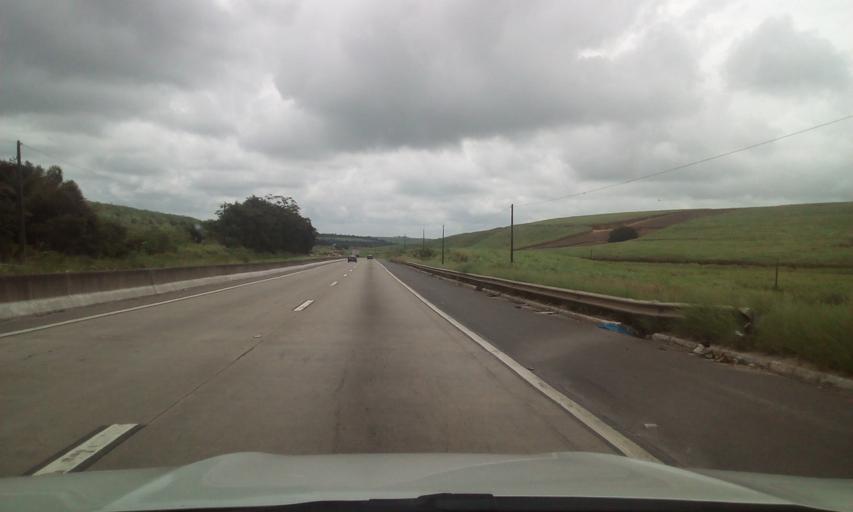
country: BR
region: Pernambuco
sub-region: Itapissuma
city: Itapissuma
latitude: -7.7836
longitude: -34.9304
